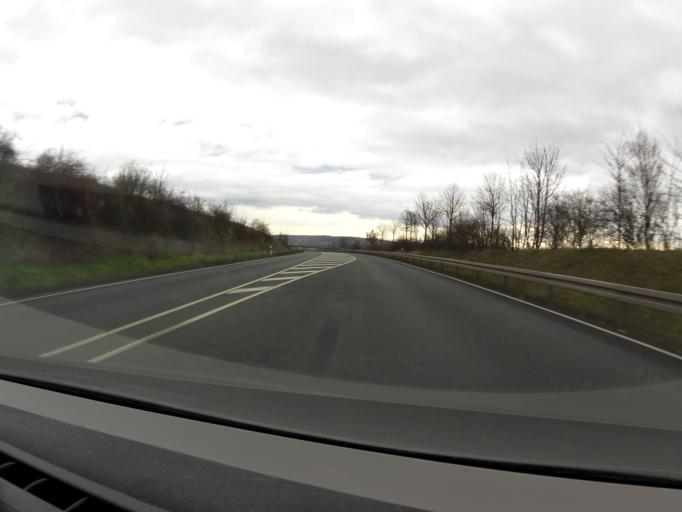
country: DE
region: Saxony-Anhalt
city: Sangerhausen
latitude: 51.4623
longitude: 11.3201
